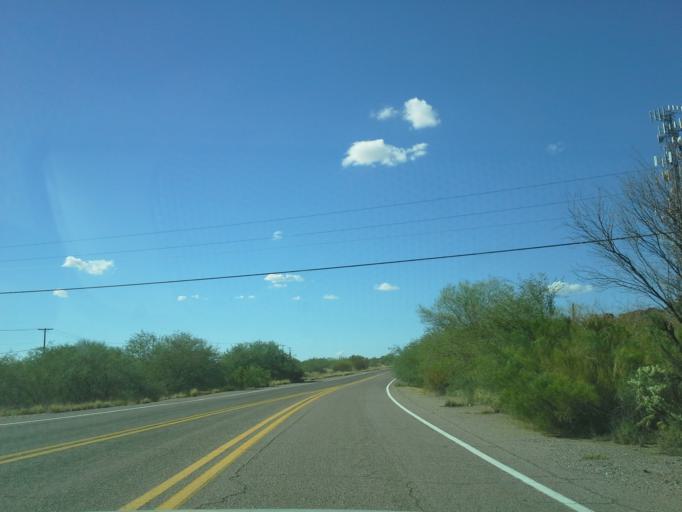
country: US
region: Arizona
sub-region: Pinal County
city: Gold Camp
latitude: 33.2590
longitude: -111.3372
